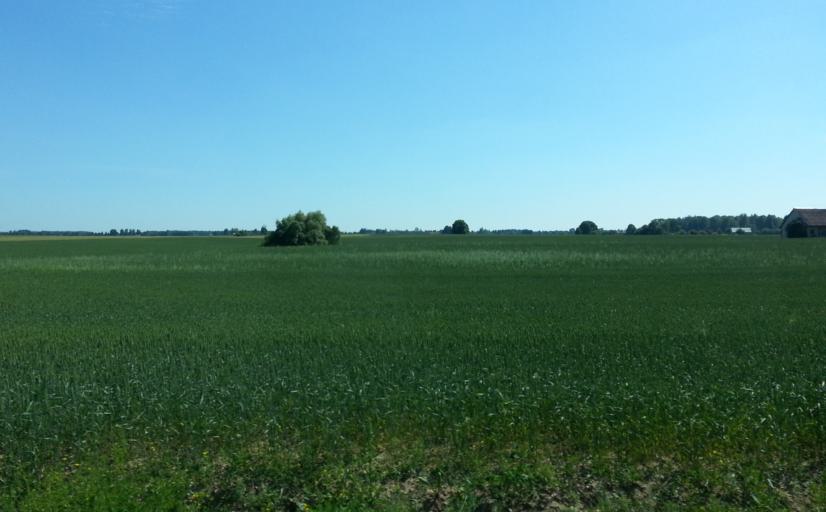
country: LT
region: Panevezys
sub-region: Birzai
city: Birzai
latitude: 56.2130
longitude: 24.6691
